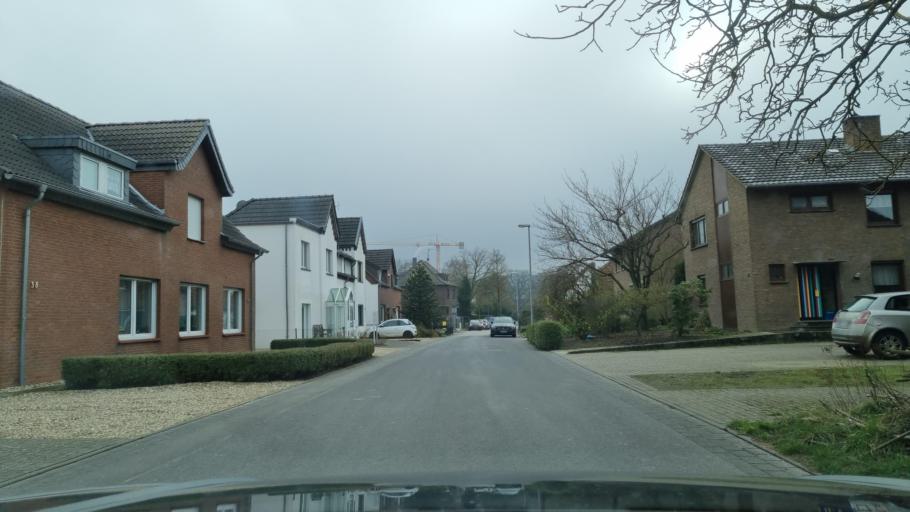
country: DE
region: North Rhine-Westphalia
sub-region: Regierungsbezirk Dusseldorf
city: Kleve
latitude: 51.8075
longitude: 6.1272
